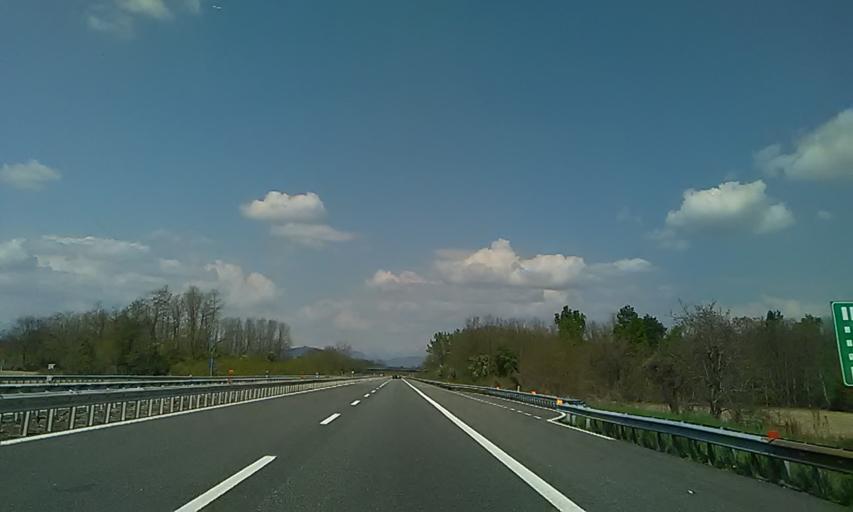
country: IT
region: Piedmont
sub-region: Provincia di Novara
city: Sizzano
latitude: 45.5729
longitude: 8.4105
